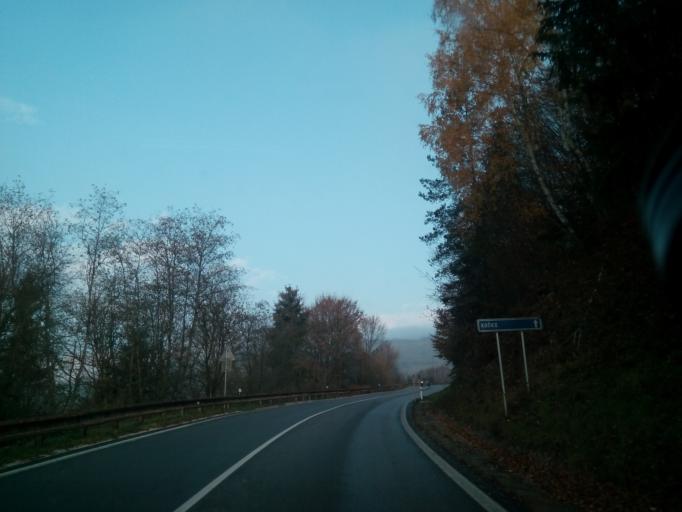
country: SK
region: Kosicky
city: Gelnica
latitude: 48.8520
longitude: 21.0158
